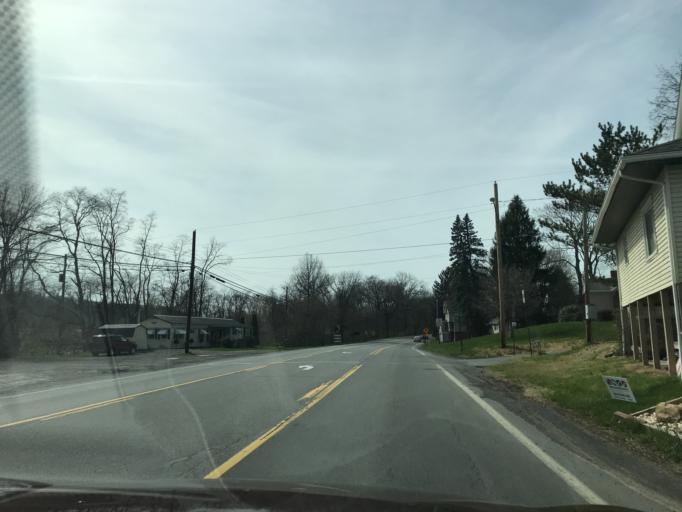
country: US
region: Pennsylvania
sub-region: Northumberland County
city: Northumberland
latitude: 40.8941
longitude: -76.8082
